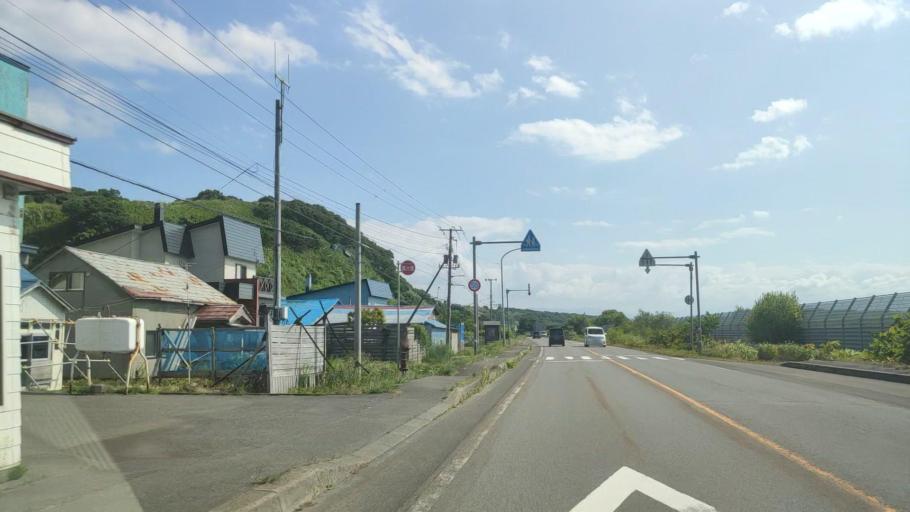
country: JP
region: Hokkaido
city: Rumoi
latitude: 43.9754
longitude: 141.6465
